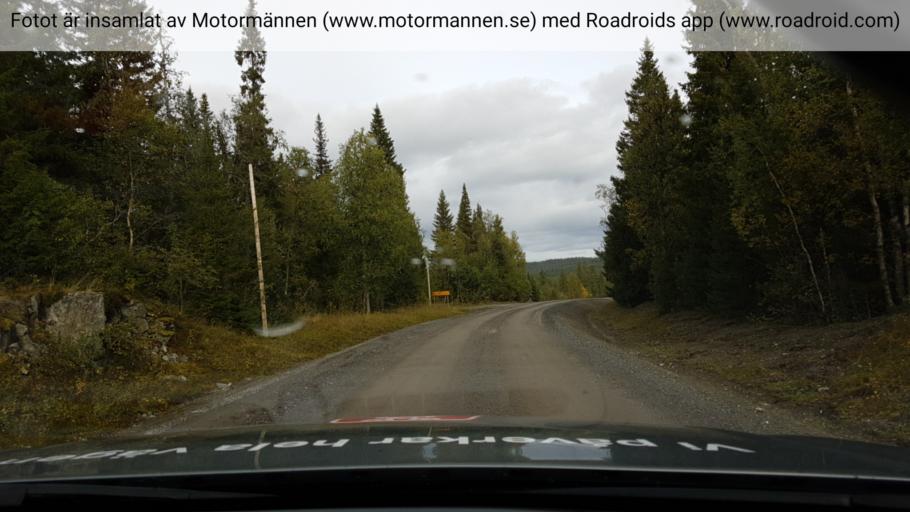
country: NO
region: Nord-Trondelag
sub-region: Snasa
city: Snaase
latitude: 63.7353
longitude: 12.4675
